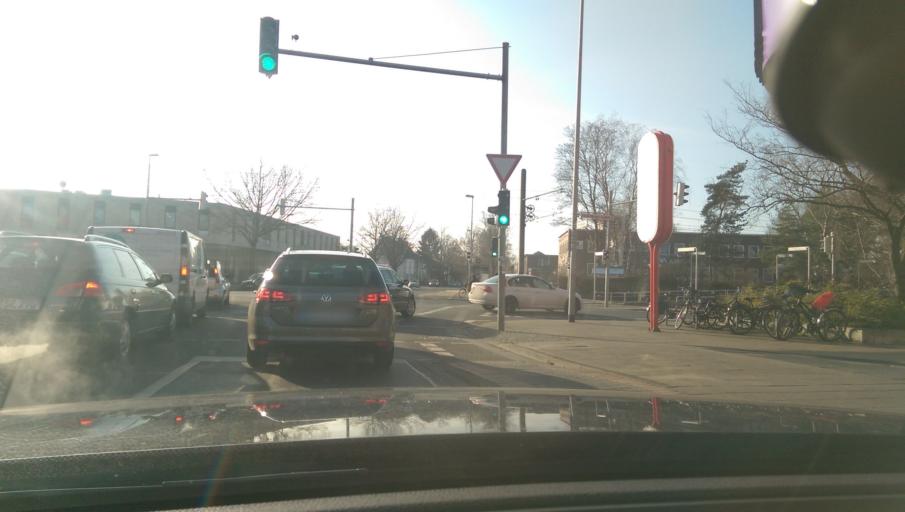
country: DE
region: Lower Saxony
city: Langenhagen
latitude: 52.4197
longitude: 9.6950
